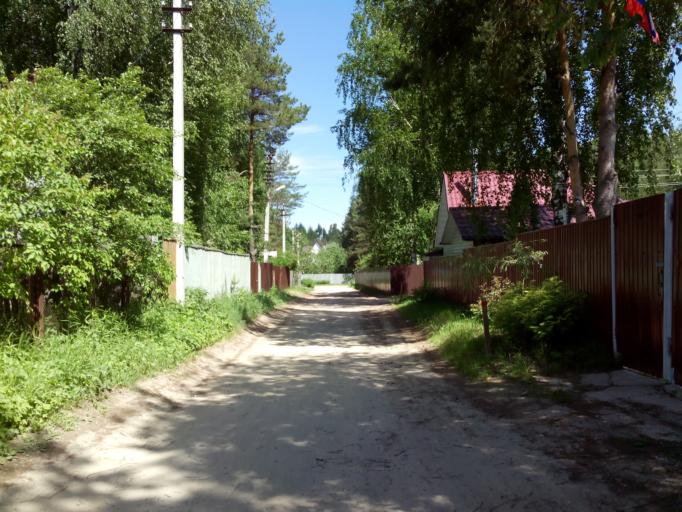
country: RU
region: Moskovskaya
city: Bogorodskoye
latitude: 56.5140
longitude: 38.1936
